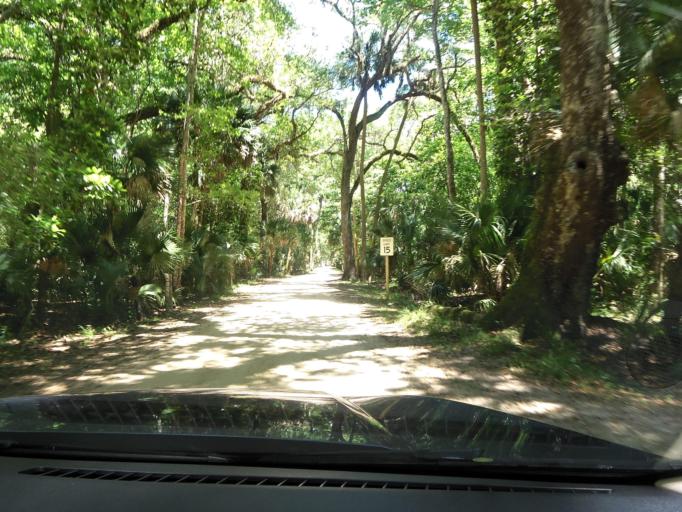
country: US
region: Florida
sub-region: Flagler County
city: Flagler Beach
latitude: 29.4324
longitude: -81.1457
